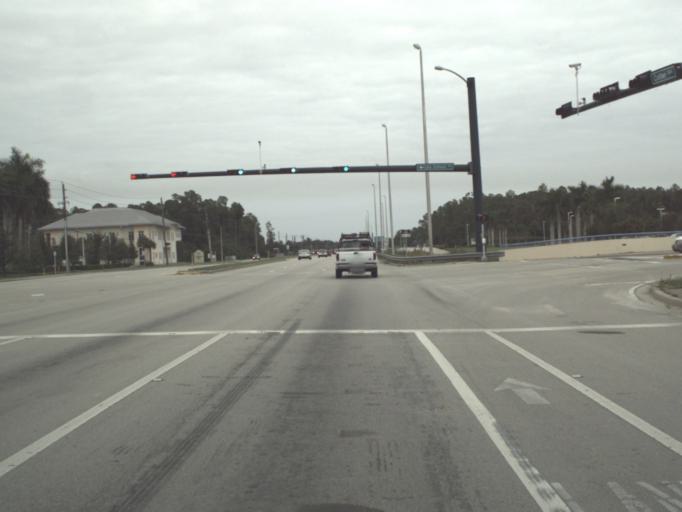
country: US
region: Florida
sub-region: Collier County
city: Lely Resort
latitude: 26.1037
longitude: -81.6871
